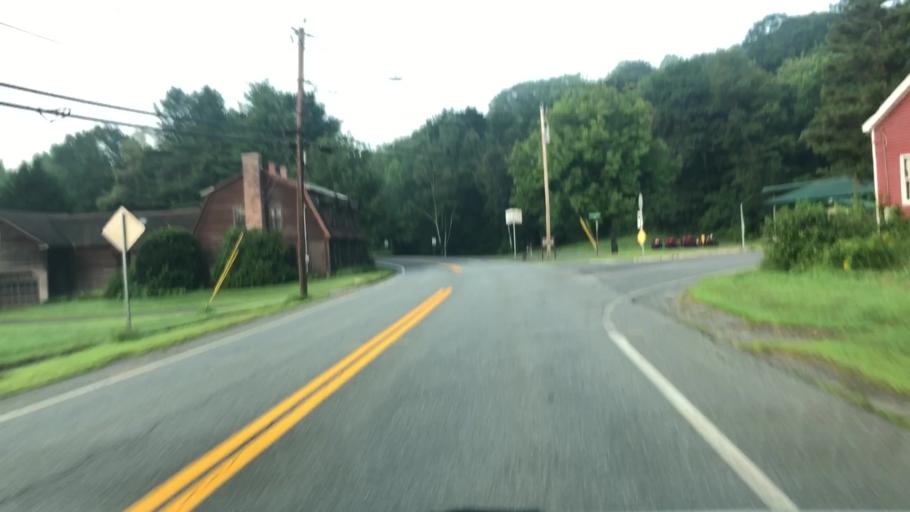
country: US
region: Massachusetts
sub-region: Franklin County
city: Buckland
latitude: 42.5653
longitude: -72.8031
